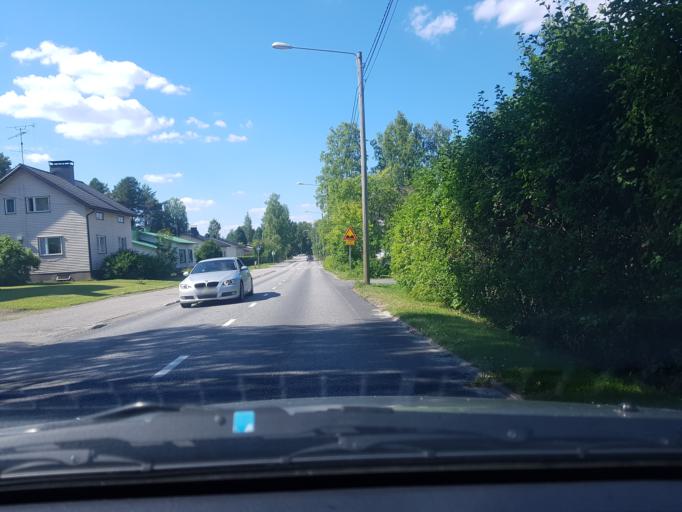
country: FI
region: Kainuu
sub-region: Kehys-Kainuu
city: Kuhmo
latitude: 64.1230
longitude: 29.5172
